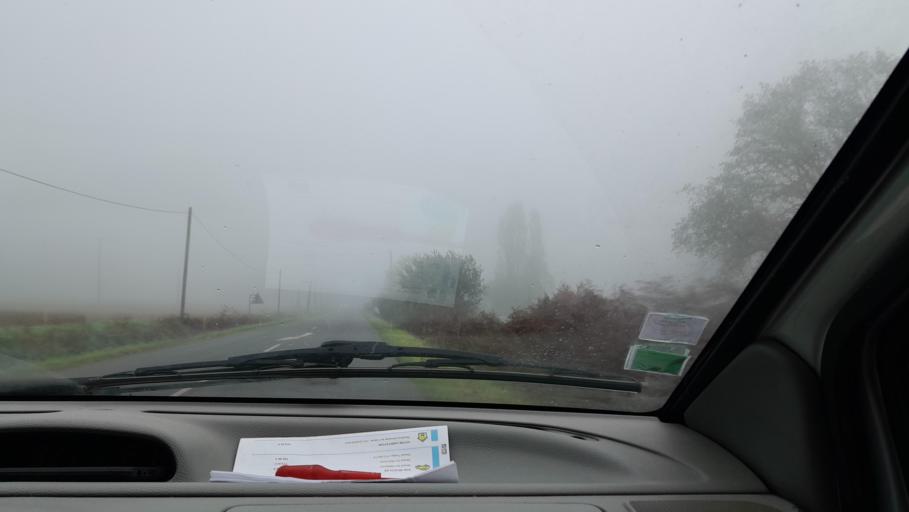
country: FR
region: Brittany
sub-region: Departement d'Ille-et-Vilaine
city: Le Pertre
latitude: 48.0174
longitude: -1.0375
